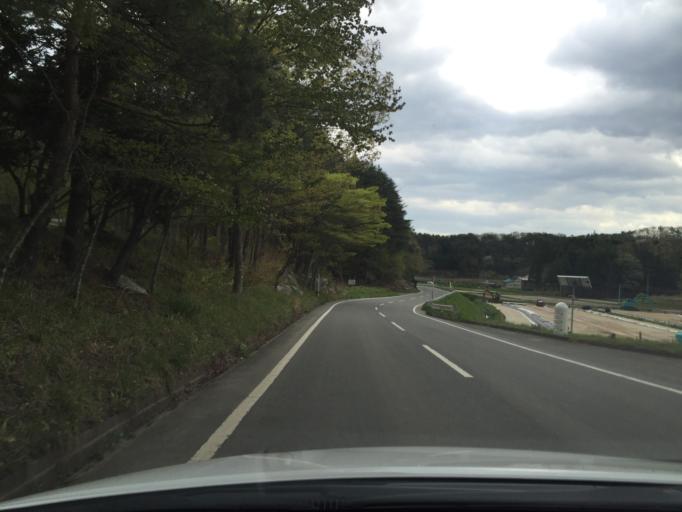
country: JP
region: Fukushima
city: Yanagawamachi-saiwaicho
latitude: 37.7098
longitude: 140.7391
